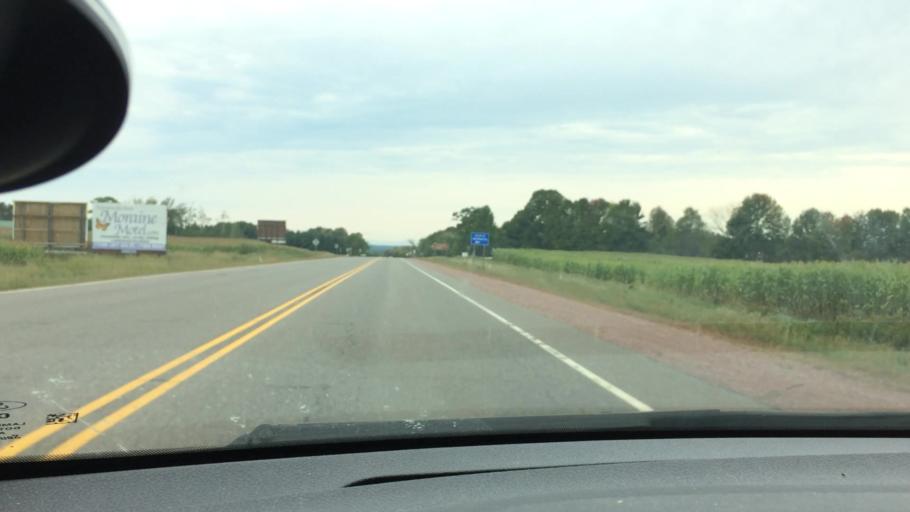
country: US
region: Wisconsin
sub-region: Clark County
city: Neillsville
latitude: 44.5637
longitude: -90.6557
